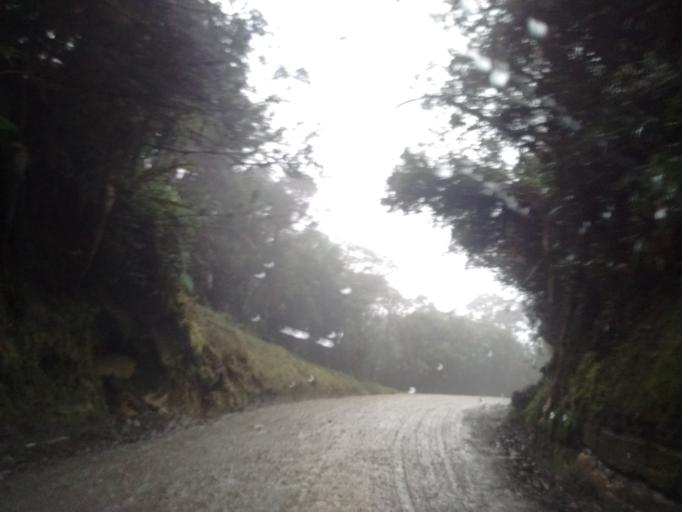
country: CO
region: Cauca
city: Paispamba
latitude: 2.1622
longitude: -76.4194
